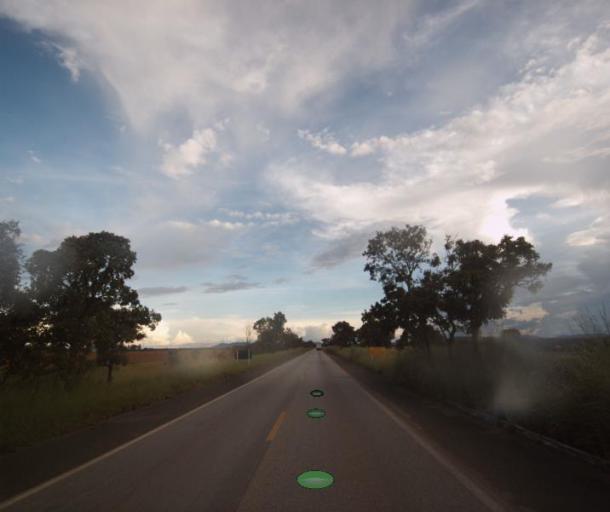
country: BR
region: Goias
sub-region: Uruacu
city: Uruacu
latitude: -14.0378
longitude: -49.0884
